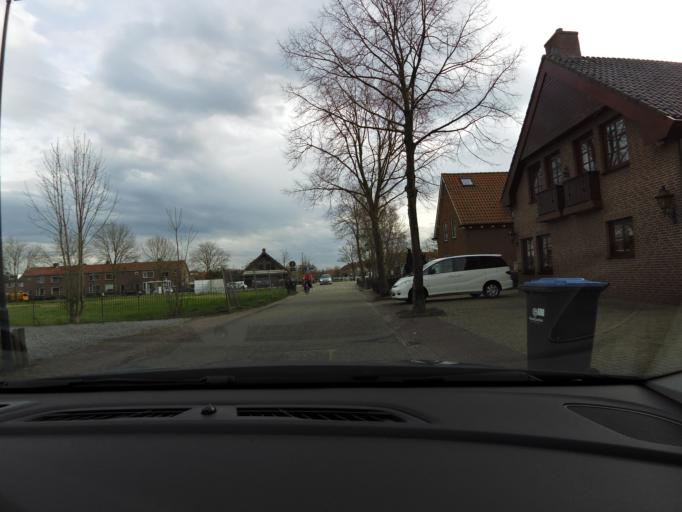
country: NL
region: South Holland
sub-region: Gemeente Gorinchem
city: Gorinchem
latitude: 51.8773
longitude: 4.9469
